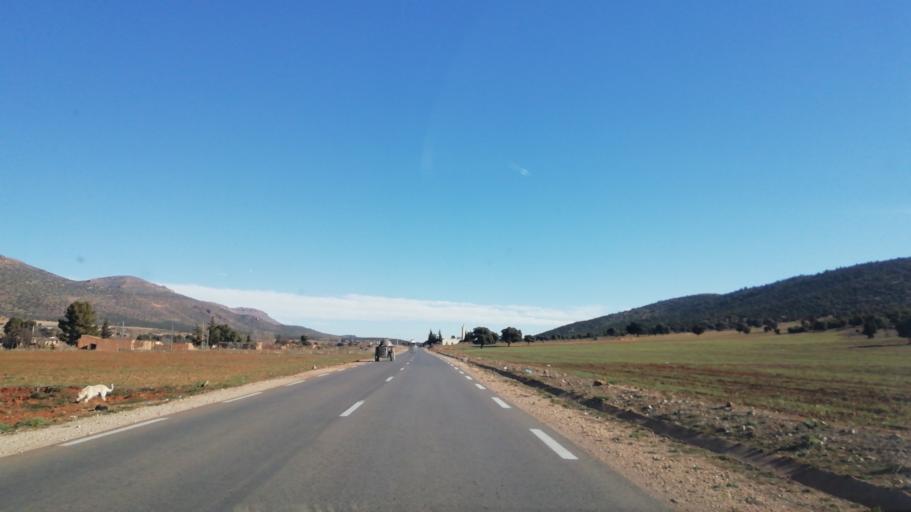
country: DZ
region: Tlemcen
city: Sebdou
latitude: 34.6873
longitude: -1.2471
